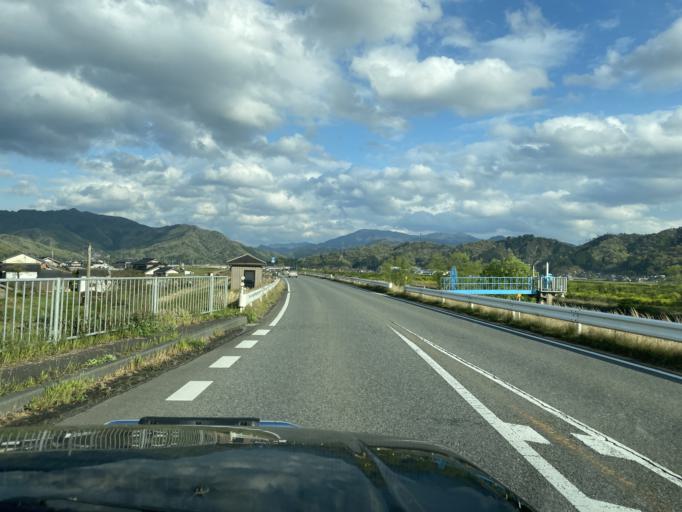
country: JP
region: Hyogo
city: Toyooka
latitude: 35.4920
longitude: 134.8427
